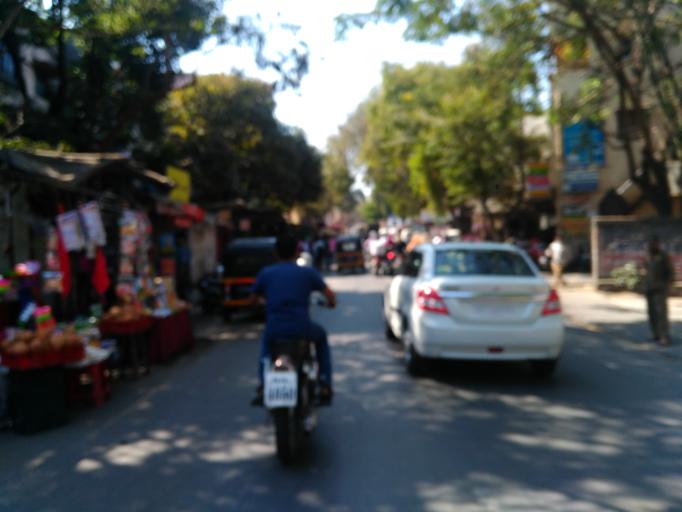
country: IN
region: Maharashtra
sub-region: Pune Division
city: Pune
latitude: 18.4926
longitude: 73.8495
